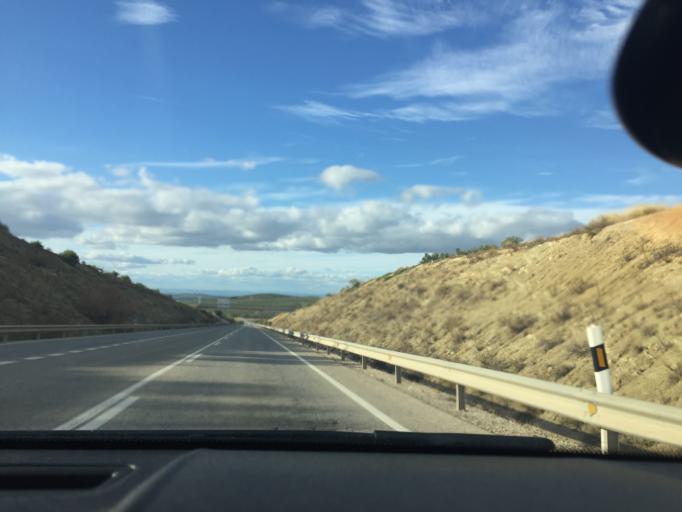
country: ES
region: Andalusia
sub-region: Provincia de Jaen
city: Torredonjimeno
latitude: 37.7607
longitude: -3.9658
